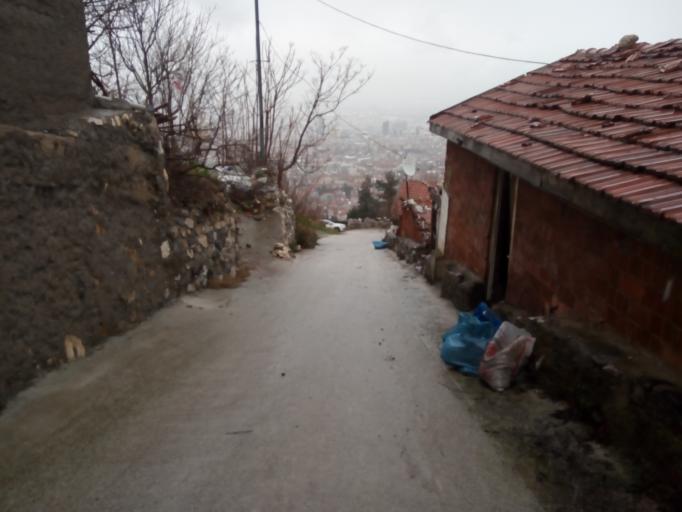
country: TR
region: Bursa
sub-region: Osmangazi
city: Bursa
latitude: 40.1742
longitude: 29.0594
